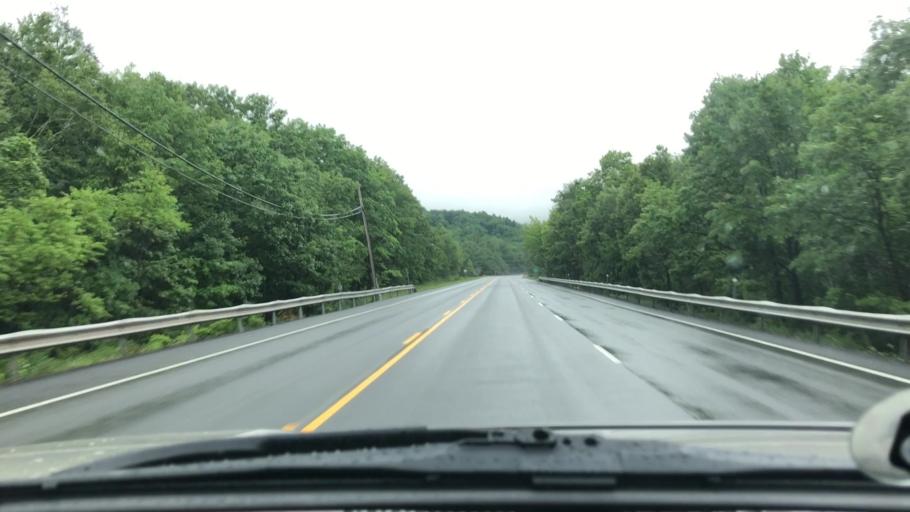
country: US
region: New York
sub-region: Greene County
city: Cairo
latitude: 42.3251
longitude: -74.1031
